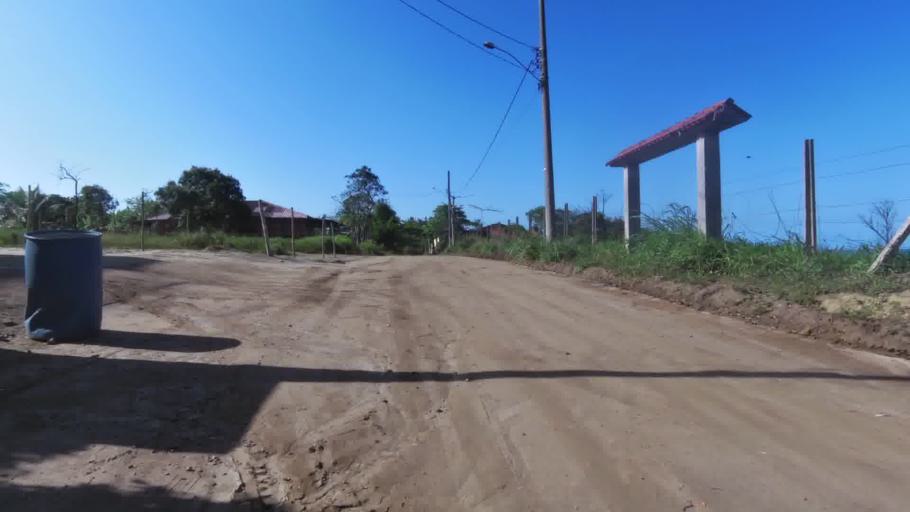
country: BR
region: Espirito Santo
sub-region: Piuma
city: Piuma
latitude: -20.8213
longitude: -40.6172
